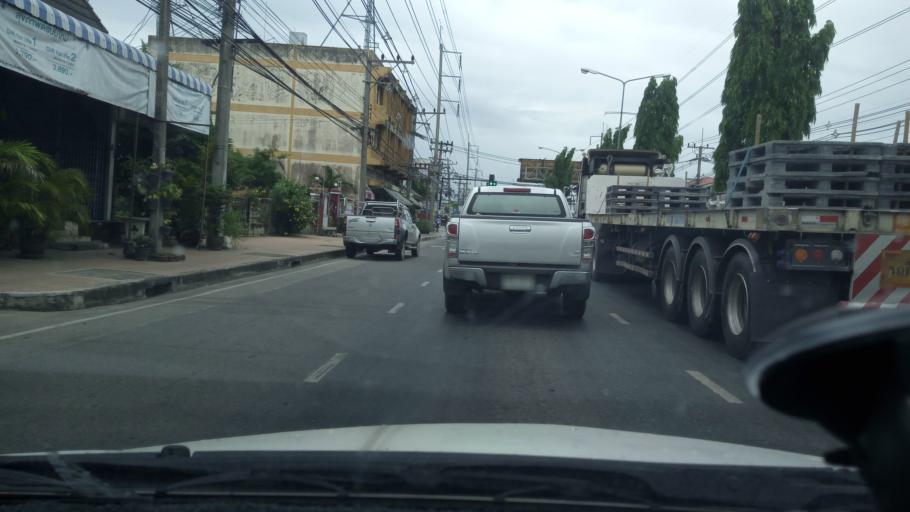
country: TH
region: Chon Buri
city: Phanat Nikhom
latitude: 13.4570
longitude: 101.1742
